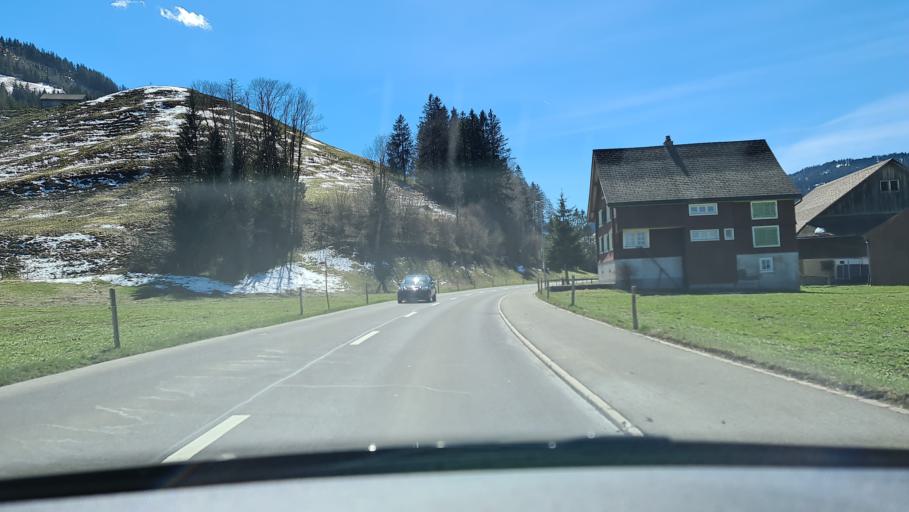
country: CH
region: Schwyz
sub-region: Bezirk Einsiedeln
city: Einsiedeln
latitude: 47.1118
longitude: 8.7357
